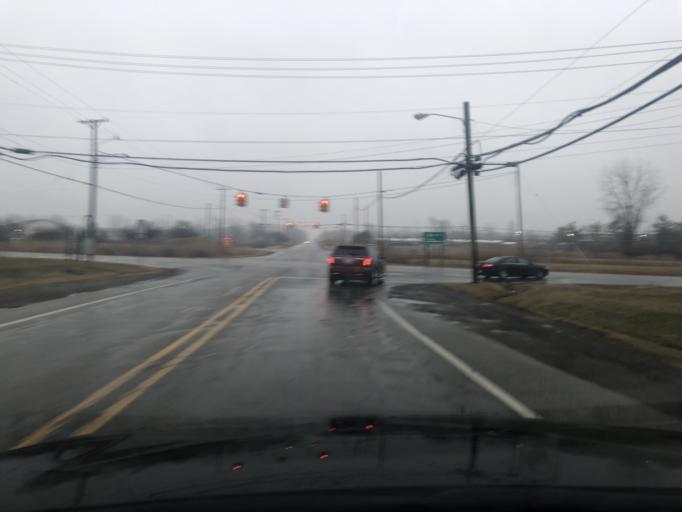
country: US
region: Michigan
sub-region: Wayne County
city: Gibraltar
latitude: 42.1119
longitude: -83.2160
